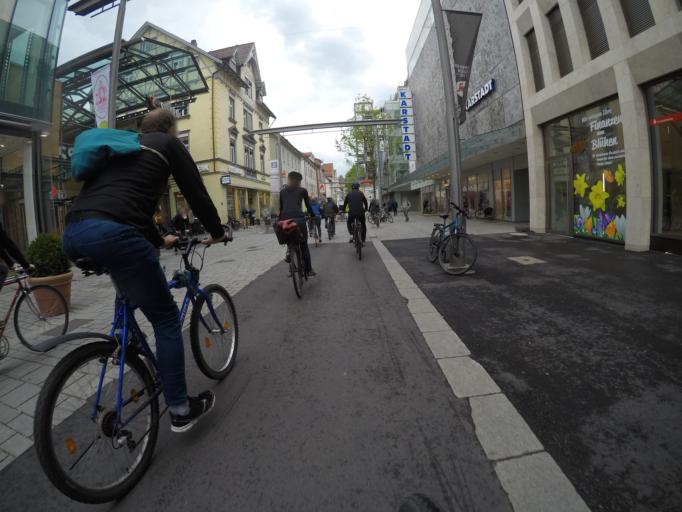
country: DE
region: Baden-Wuerttemberg
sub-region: Regierungsbezirk Stuttgart
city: Esslingen
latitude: 48.7395
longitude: 9.3023
